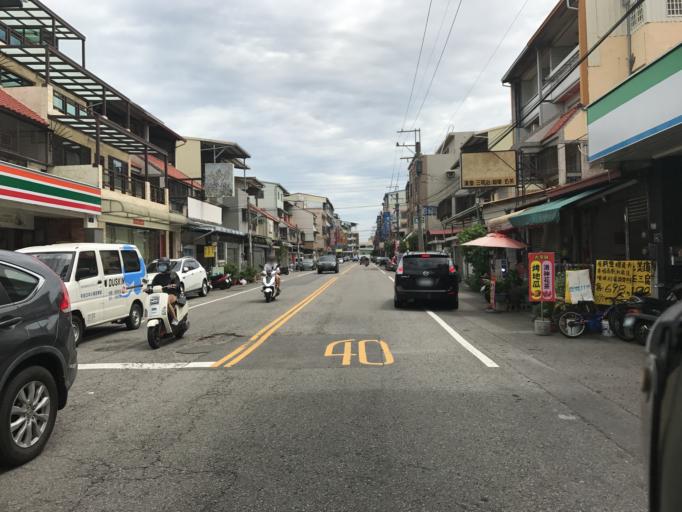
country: TW
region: Taiwan
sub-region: Taichung City
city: Taichung
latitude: 24.0860
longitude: 120.7018
